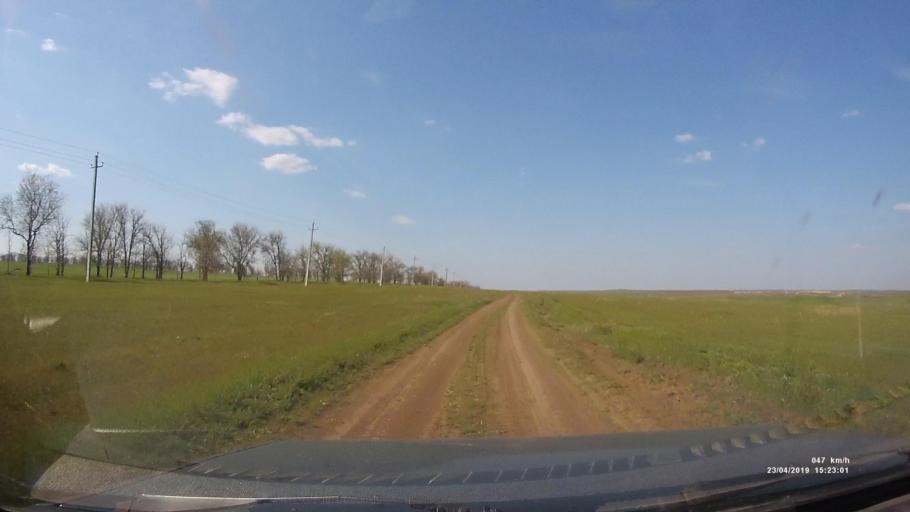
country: RU
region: Rostov
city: Remontnoye
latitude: 46.5327
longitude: 42.9698
